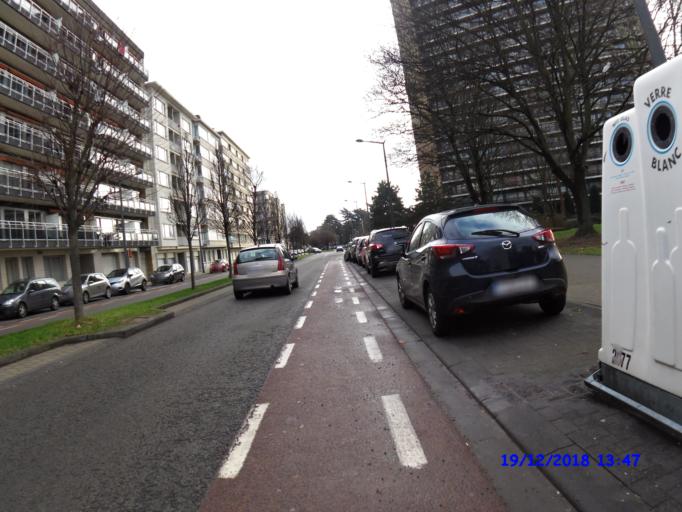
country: BE
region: Brussels Capital
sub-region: Bruxelles-Capitale
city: Brussels
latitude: 50.8626
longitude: 4.3143
